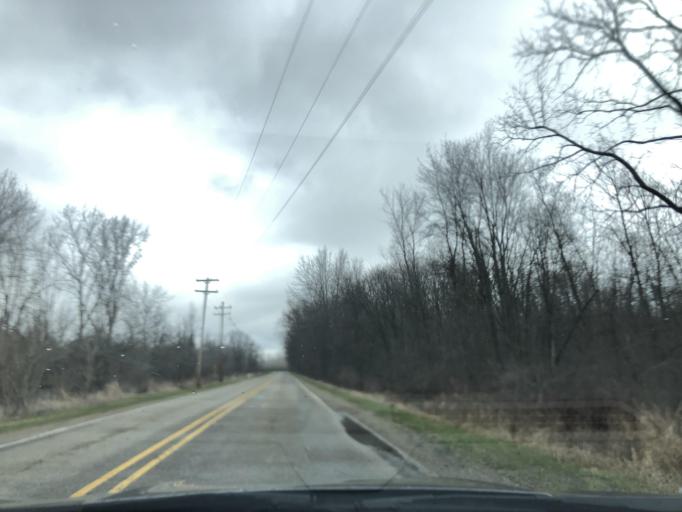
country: US
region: Michigan
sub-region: Clinton County
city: Fowler
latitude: 43.1099
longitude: -84.6933
